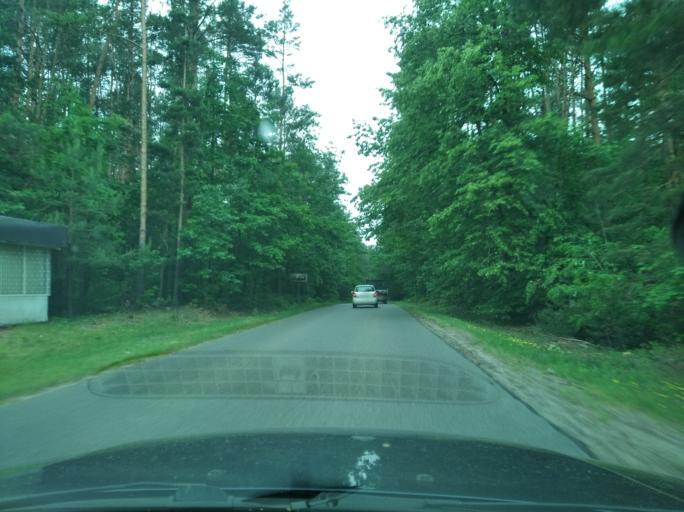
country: PL
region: Subcarpathian Voivodeship
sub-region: Powiat kolbuszowski
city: Niwiska
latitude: 50.1751
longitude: 21.6642
